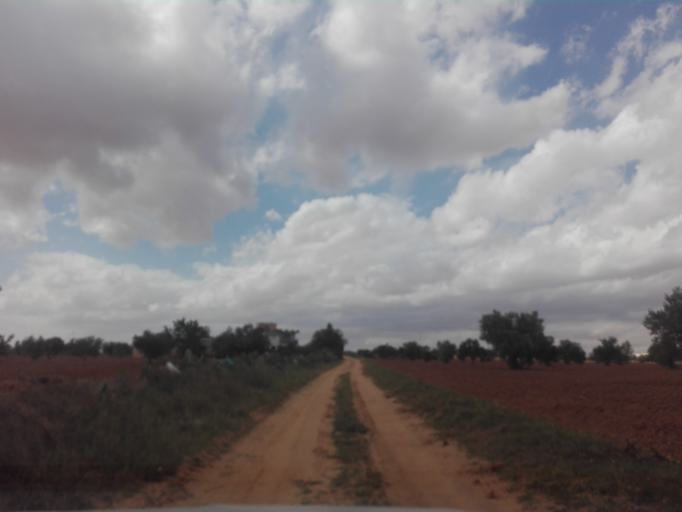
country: TN
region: Safaqis
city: Sfax
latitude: 34.6945
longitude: 10.4469
